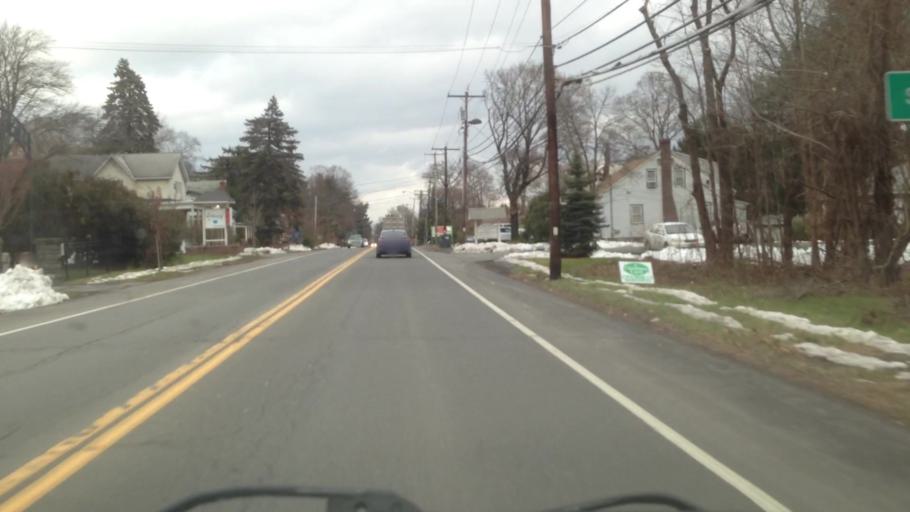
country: US
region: New York
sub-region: Ulster County
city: Saugerties South
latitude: 42.0620
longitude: -73.9509
